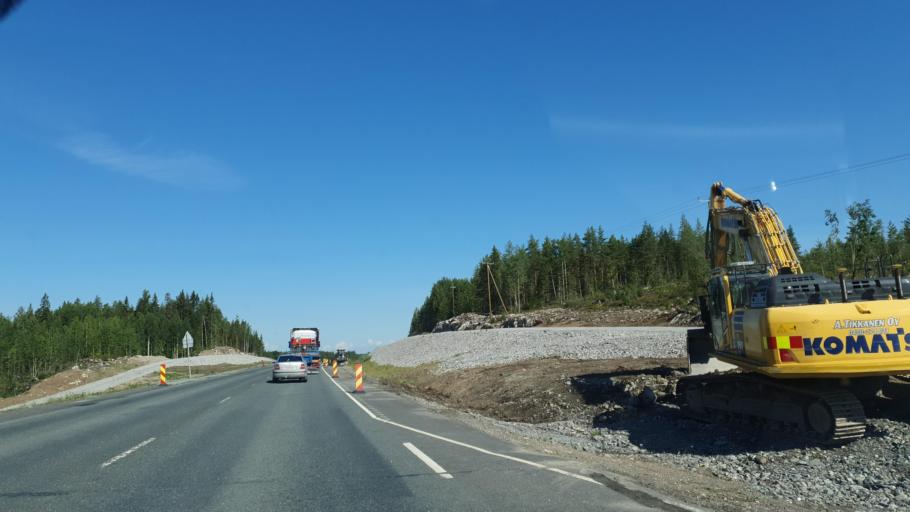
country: FI
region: Northern Savo
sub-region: Ylae-Savo
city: Lapinlahti
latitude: 63.2798
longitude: 27.4568
